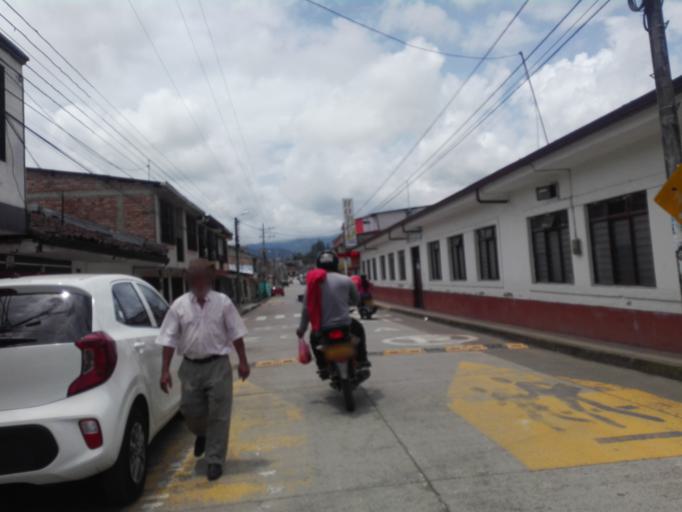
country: CO
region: Cauca
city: Rosas
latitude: 2.3523
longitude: -76.6815
